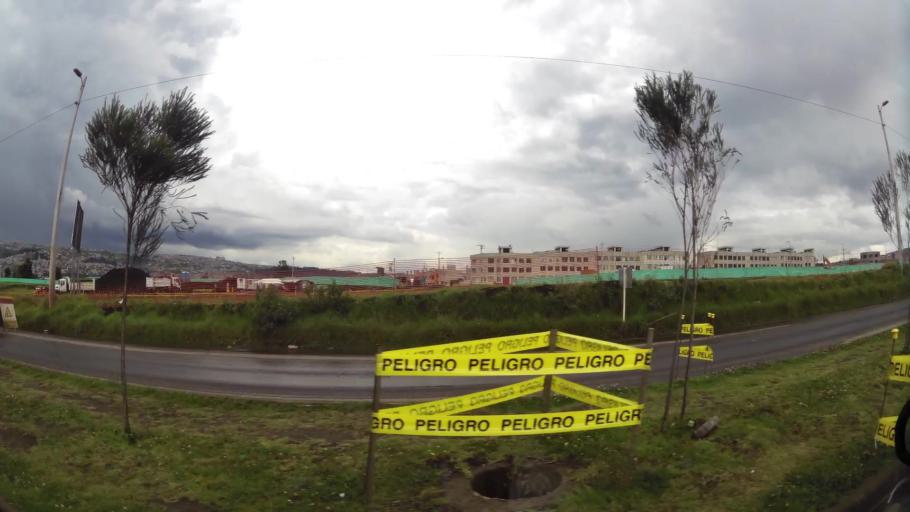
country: EC
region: Pichincha
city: Quito
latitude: -0.2988
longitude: -78.5547
